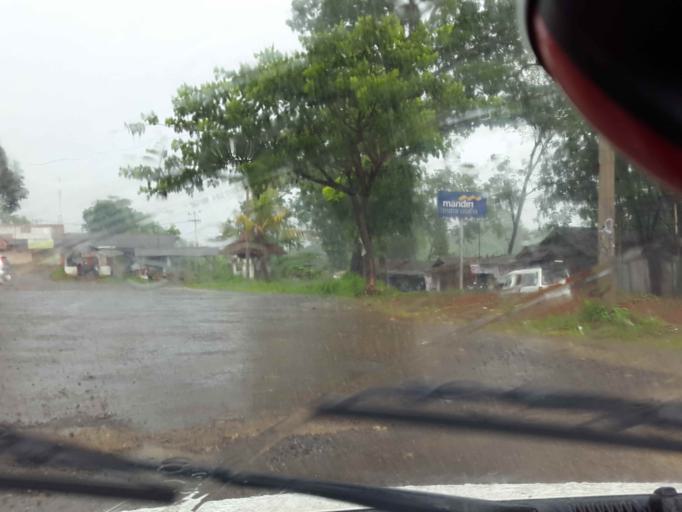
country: ID
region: West Java
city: Cilandak
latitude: -6.9797
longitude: 106.7157
